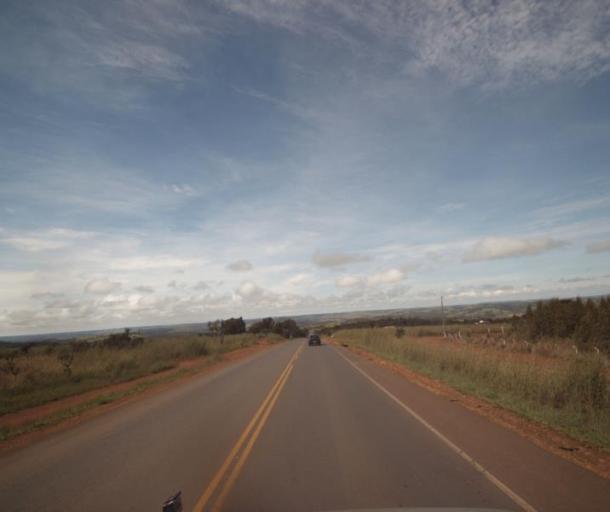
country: BR
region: Goias
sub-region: Abadiania
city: Abadiania
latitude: -16.0667
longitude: -48.8541
